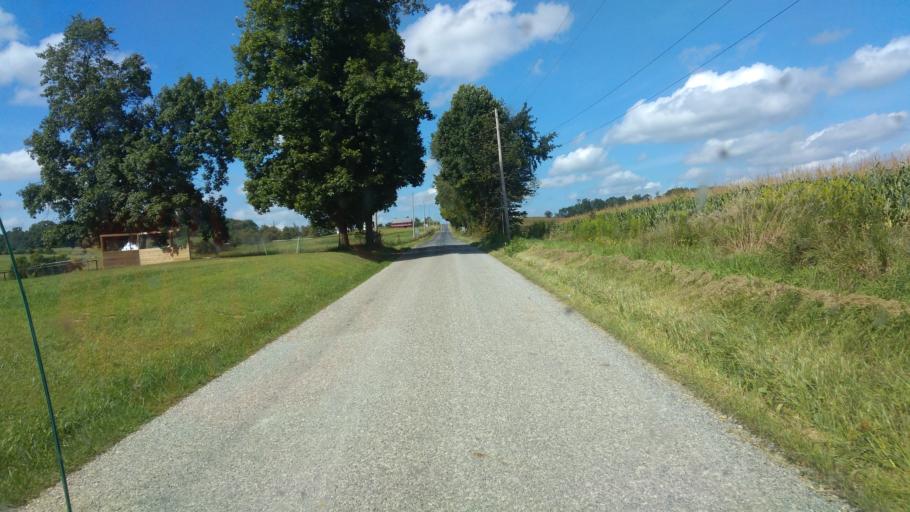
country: US
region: Ohio
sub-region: Holmes County
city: Millersburg
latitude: 40.6326
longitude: -81.8517
